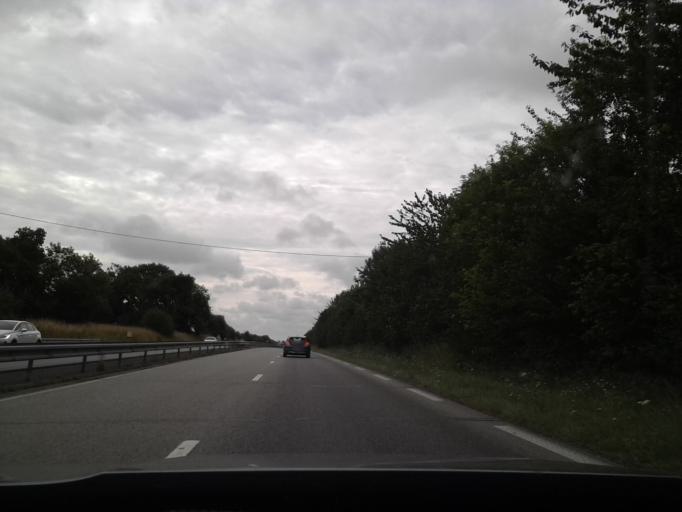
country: FR
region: Lower Normandy
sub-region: Departement de la Manche
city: Carentan
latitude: 49.3416
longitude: -1.2715
